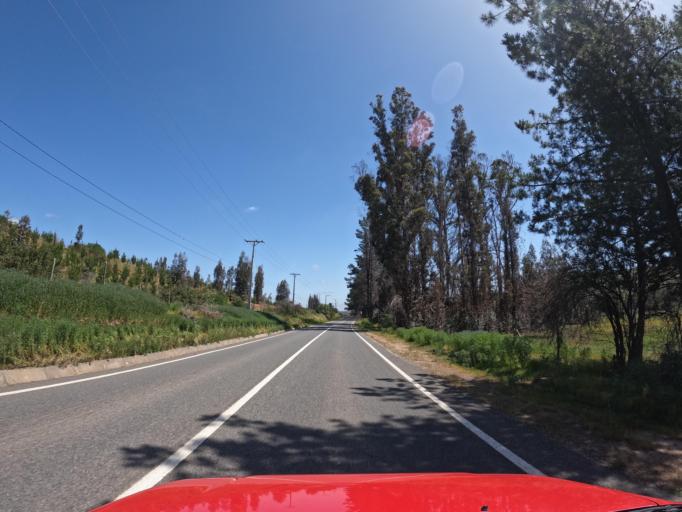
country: CL
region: O'Higgins
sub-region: Provincia de Colchagua
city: Santa Cruz
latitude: -34.6643
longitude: -71.8342
